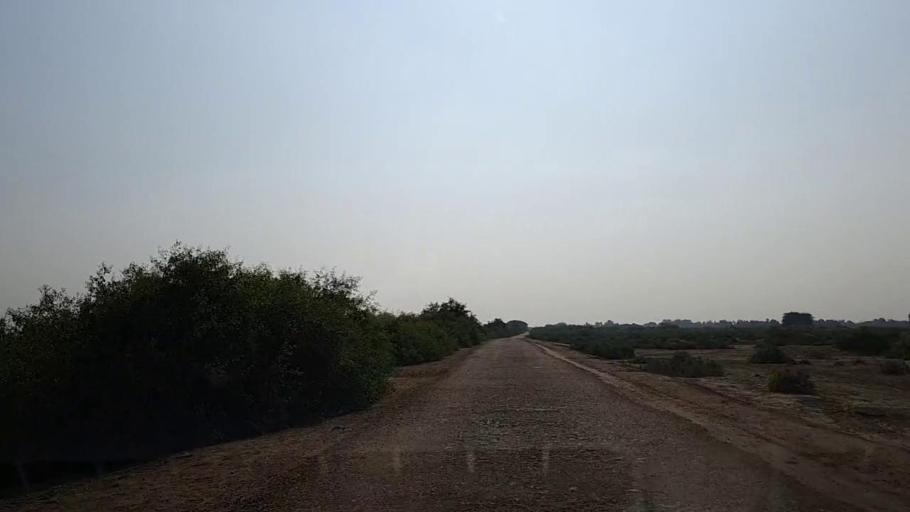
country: PK
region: Sindh
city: Mirpur Sakro
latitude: 24.6358
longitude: 67.6604
